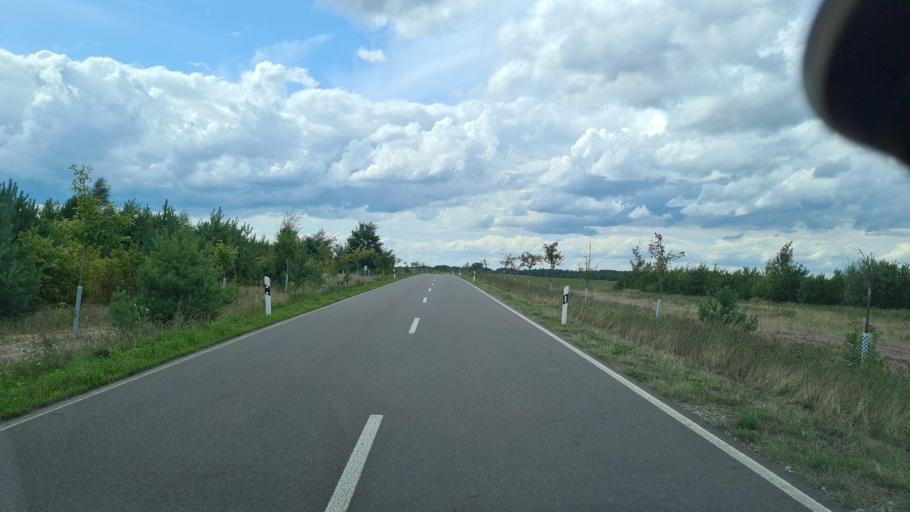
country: DE
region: Brandenburg
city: Drebkau
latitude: 51.6130
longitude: 14.2654
